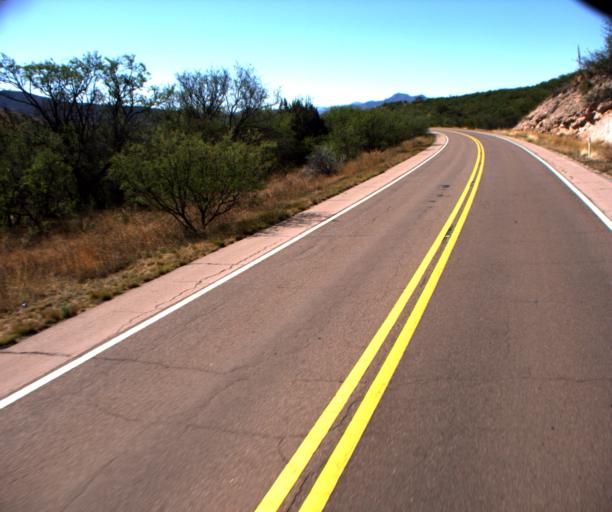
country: US
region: Arizona
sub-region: Santa Cruz County
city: Rio Rico
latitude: 31.6504
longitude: -110.7154
